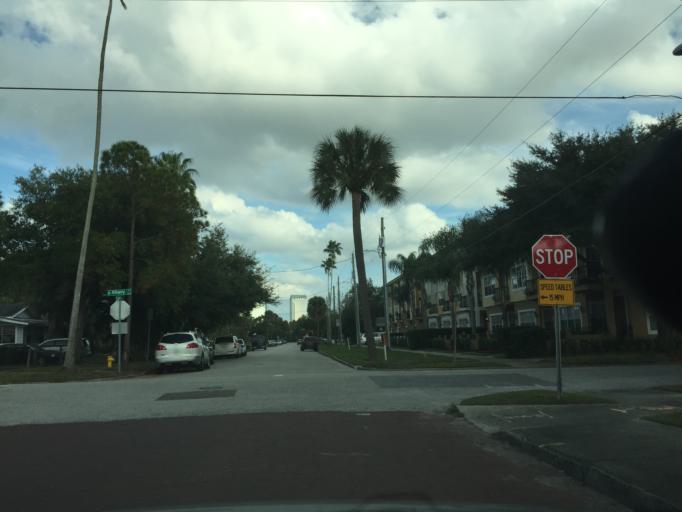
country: US
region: Florida
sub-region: Hillsborough County
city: Tampa
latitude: 27.9458
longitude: -82.4810
